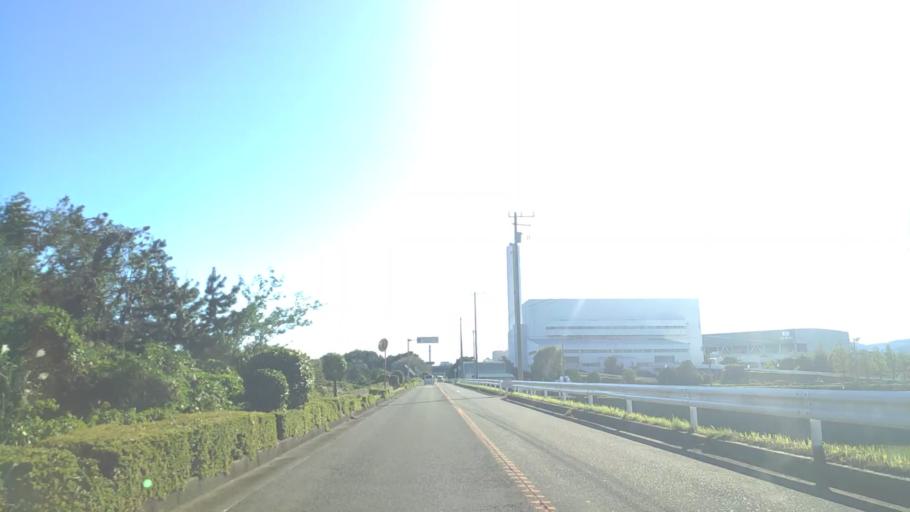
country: JP
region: Kanagawa
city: Atsugi
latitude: 35.4595
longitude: 139.3758
